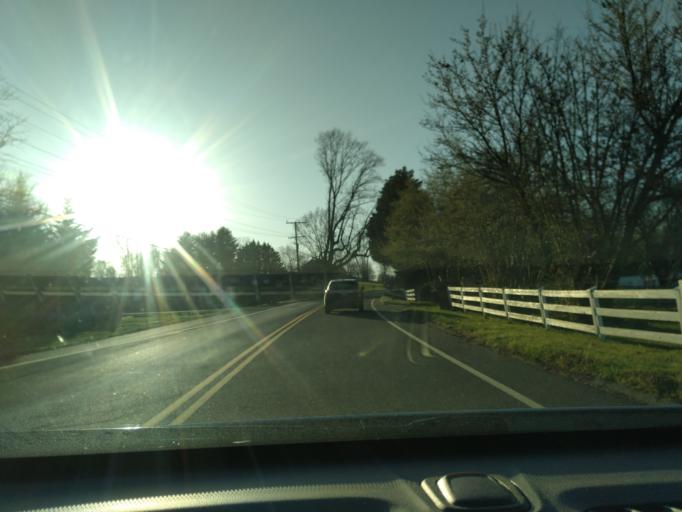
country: US
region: Maryland
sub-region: Anne Arundel County
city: Deale
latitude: 38.7774
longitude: -76.5707
